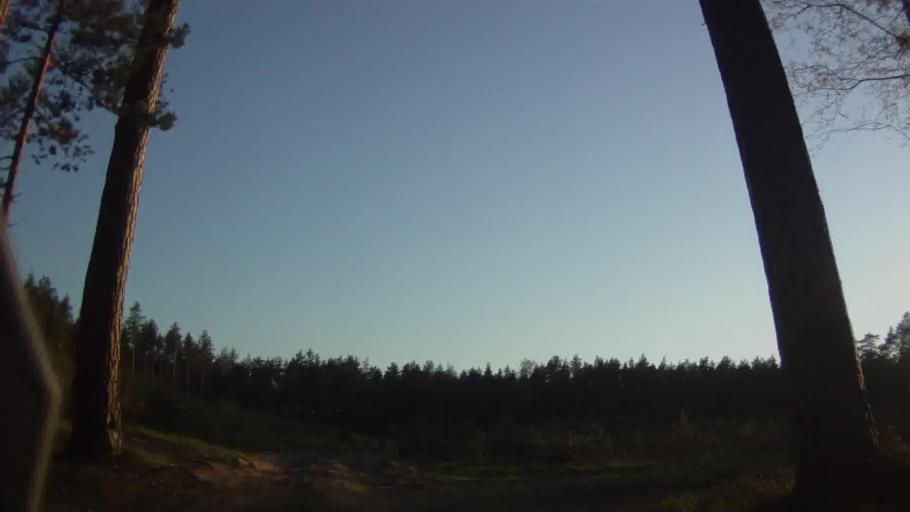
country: LV
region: Riga
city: Jaunciems
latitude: 57.0613
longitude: 24.1702
